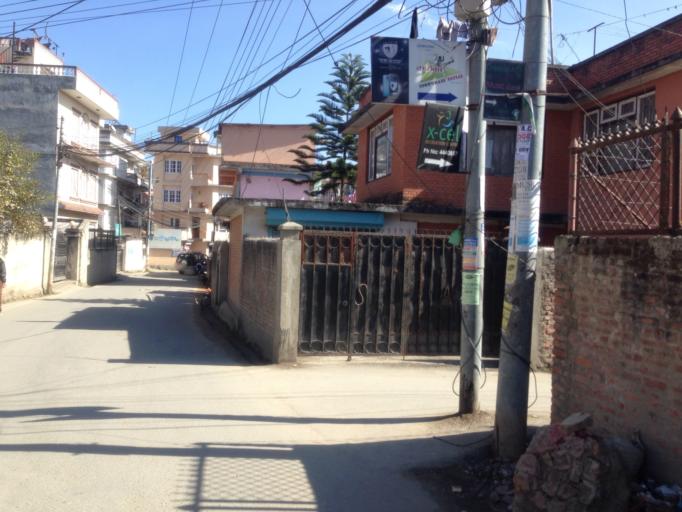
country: NP
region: Central Region
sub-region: Bagmati Zone
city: Kathmandu
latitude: 27.7240
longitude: 85.3327
